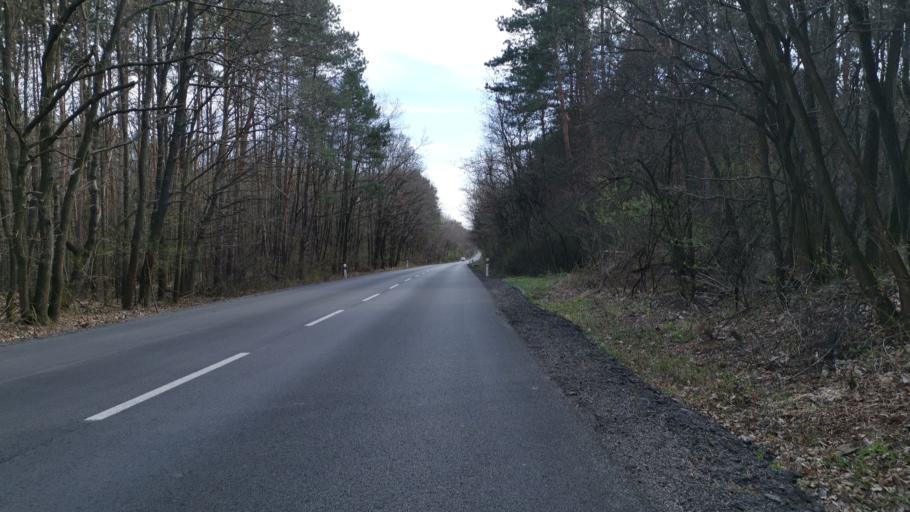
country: SK
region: Trnavsky
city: Gbely
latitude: 48.7020
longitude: 17.1244
